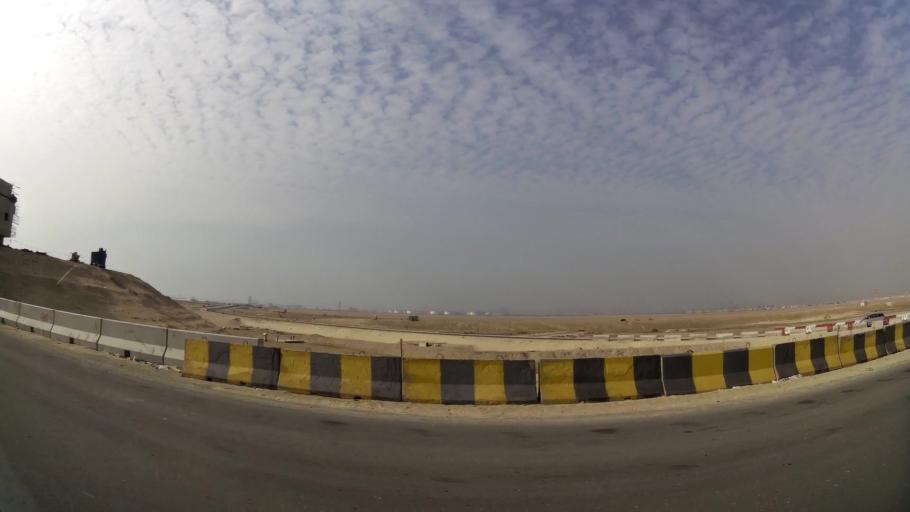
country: AE
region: Abu Dhabi
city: Abu Dhabi
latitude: 24.2785
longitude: 54.5240
